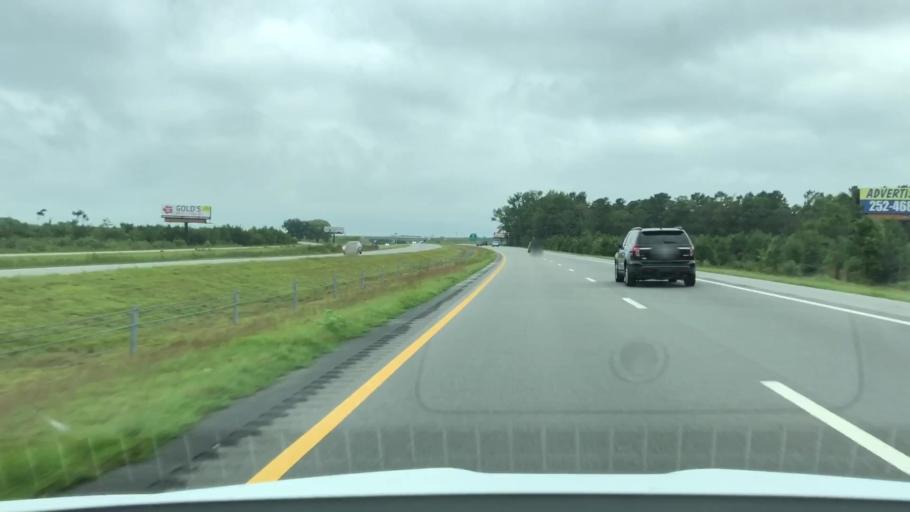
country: US
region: North Carolina
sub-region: Wayne County
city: Elroy
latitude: 35.3998
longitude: -77.8721
